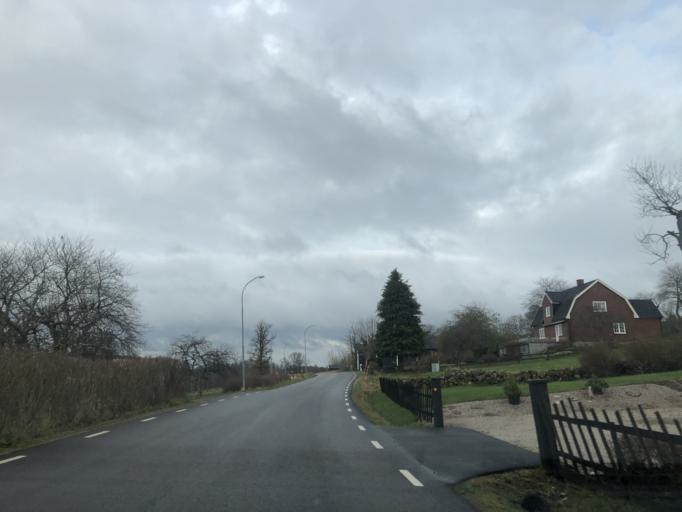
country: SE
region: Vaestra Goetaland
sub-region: Ulricehamns Kommun
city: Ulricehamn
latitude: 57.8161
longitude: 13.2440
